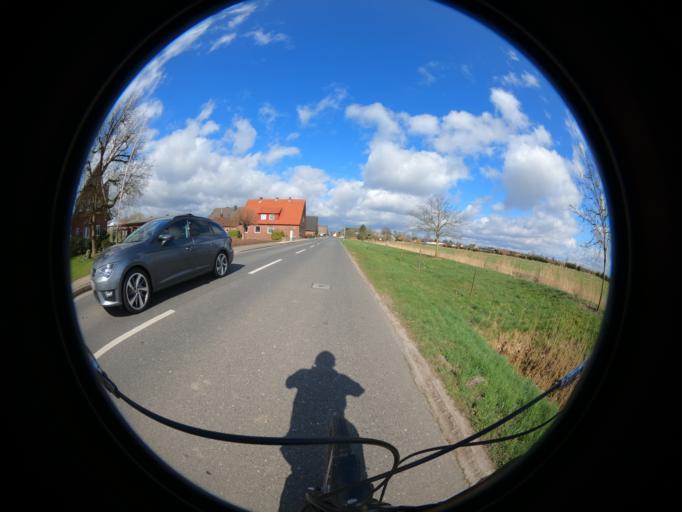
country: DE
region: Lower Saxony
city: Neu Wulmstorf
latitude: 53.5122
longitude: 9.7916
